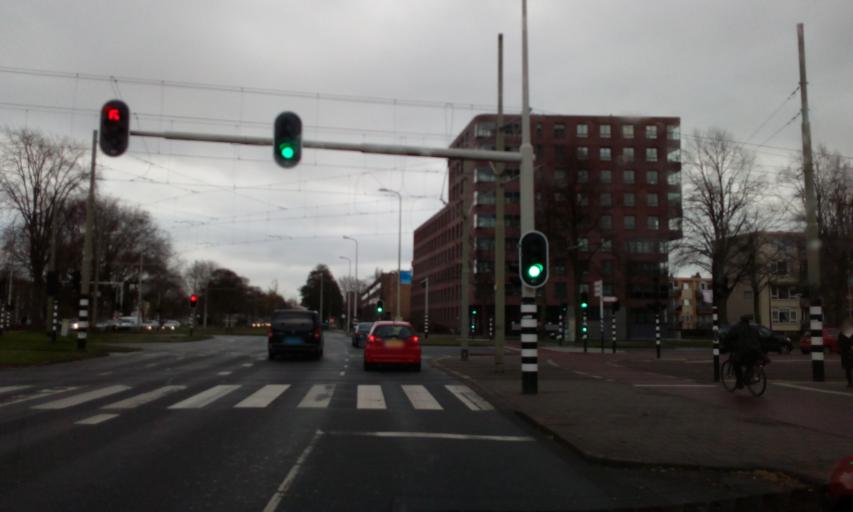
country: NL
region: South Holland
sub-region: Gemeente Den Haag
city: The Hague
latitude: 52.0489
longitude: 4.2837
